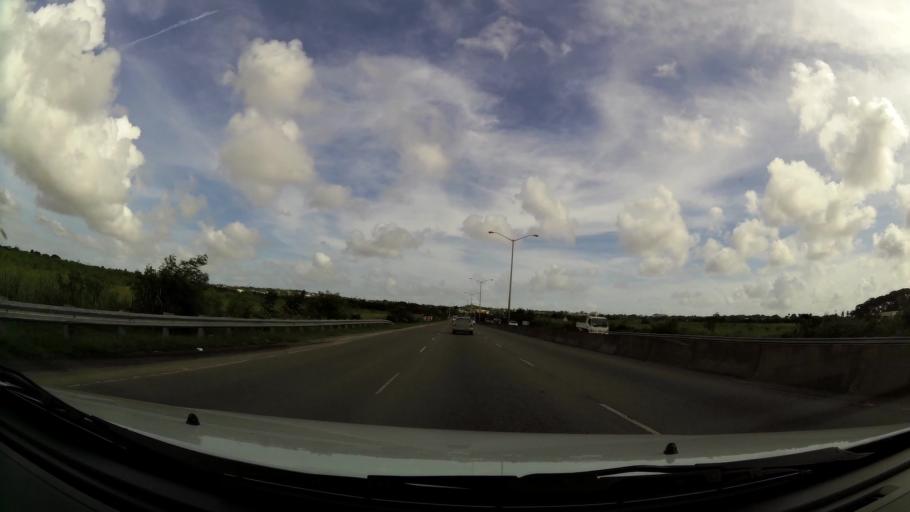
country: BB
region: Saint Michael
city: Bridgetown
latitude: 13.1175
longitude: -59.5869
